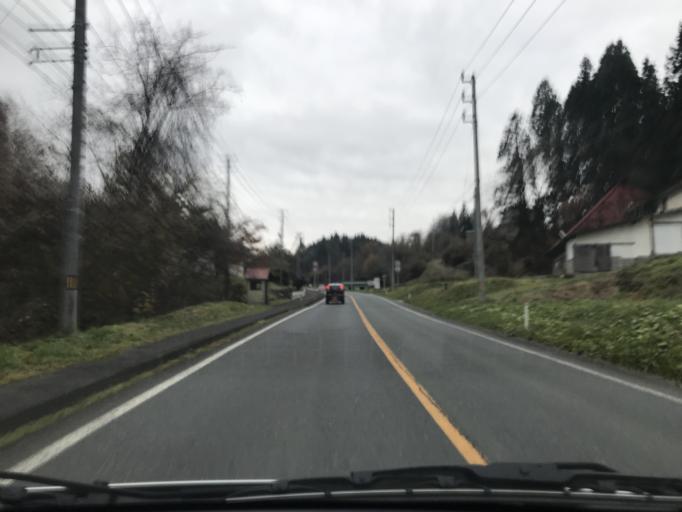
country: JP
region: Iwate
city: Ichinoseki
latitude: 39.0159
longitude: 141.3292
